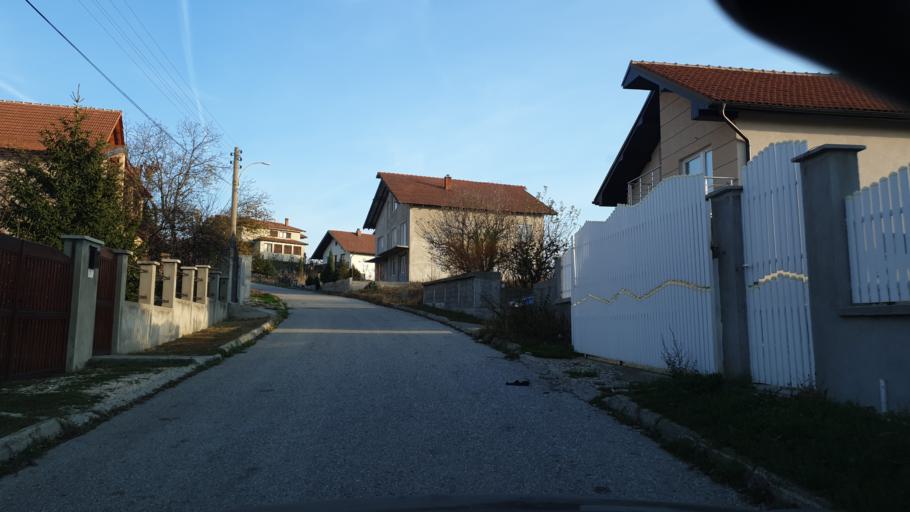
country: RS
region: Central Serbia
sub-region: Borski Okrug
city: Bor
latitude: 44.0576
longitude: 22.0798
